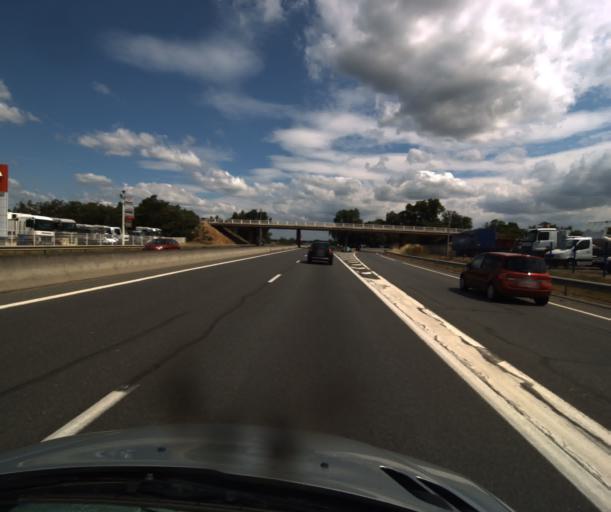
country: FR
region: Midi-Pyrenees
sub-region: Departement du Tarn-et-Garonne
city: Bressols
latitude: 43.9776
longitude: 1.3339
